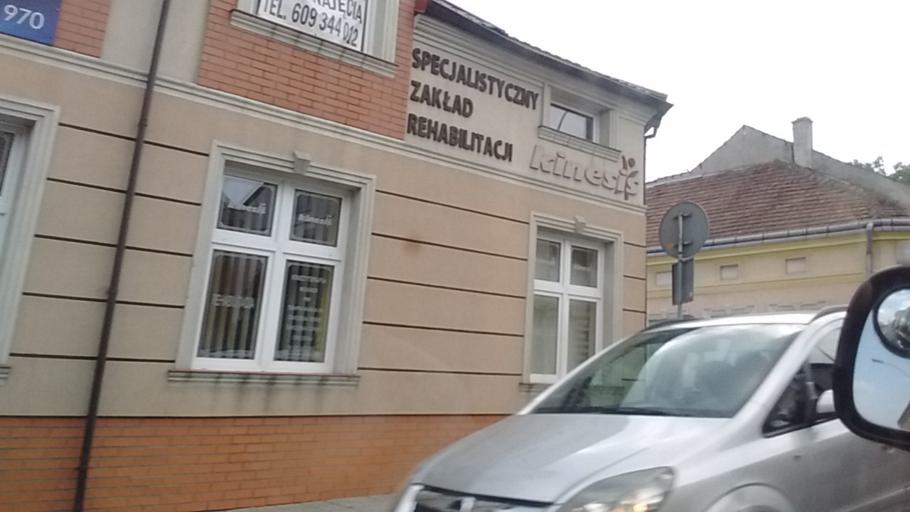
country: PL
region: Subcarpathian Voivodeship
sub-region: Powiat lezajski
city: Lezajsk
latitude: 50.2521
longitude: 22.4205
